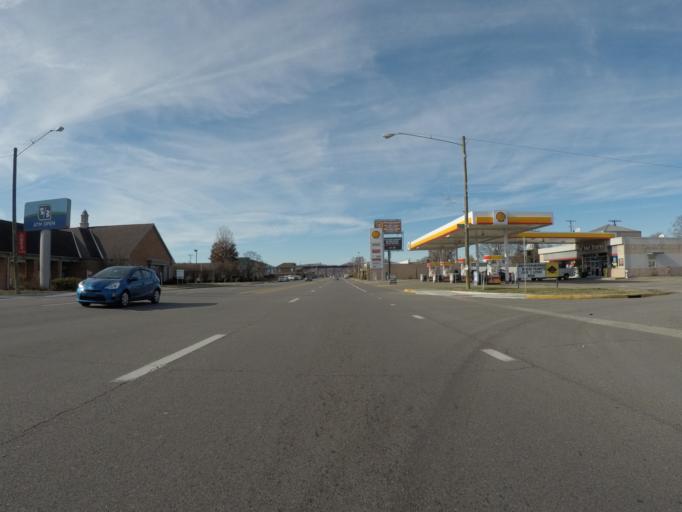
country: US
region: West Virginia
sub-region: Wayne County
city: Kenova
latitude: 38.3991
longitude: -82.5708
